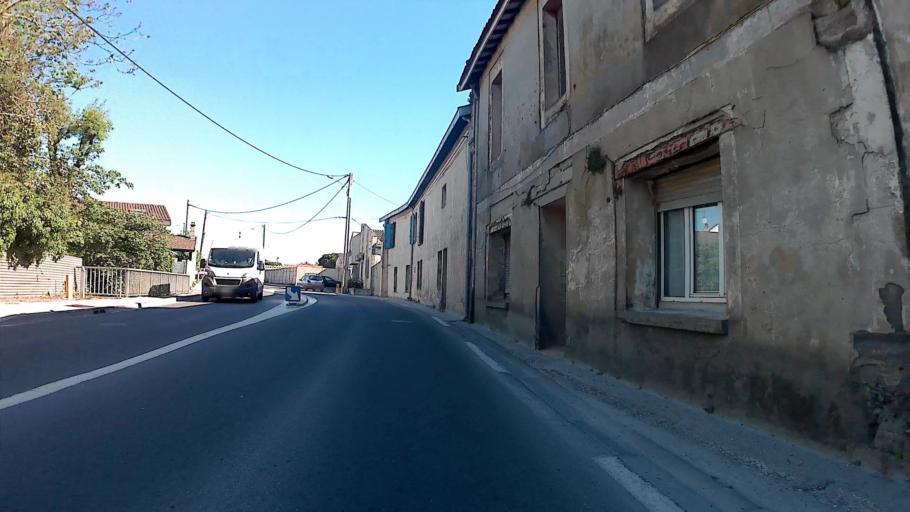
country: FR
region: Aquitaine
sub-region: Departement de la Gironde
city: Villenave-d'Ornon
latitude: 44.7713
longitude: -0.5282
